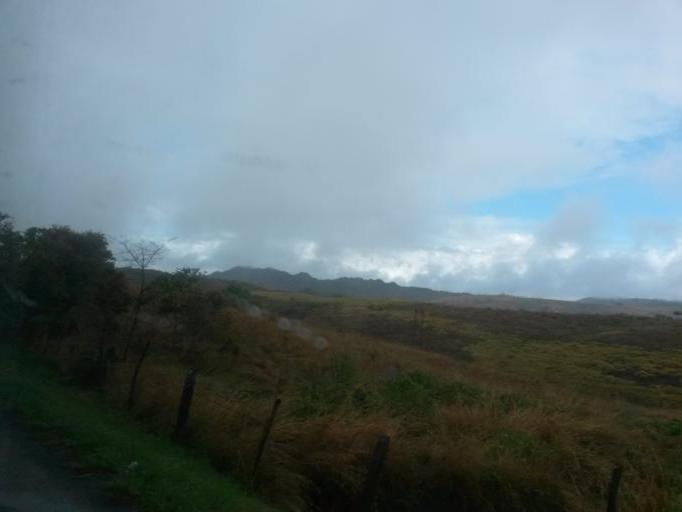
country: CO
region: Cauca
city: El Bordo
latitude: 2.1512
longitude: -76.9169
